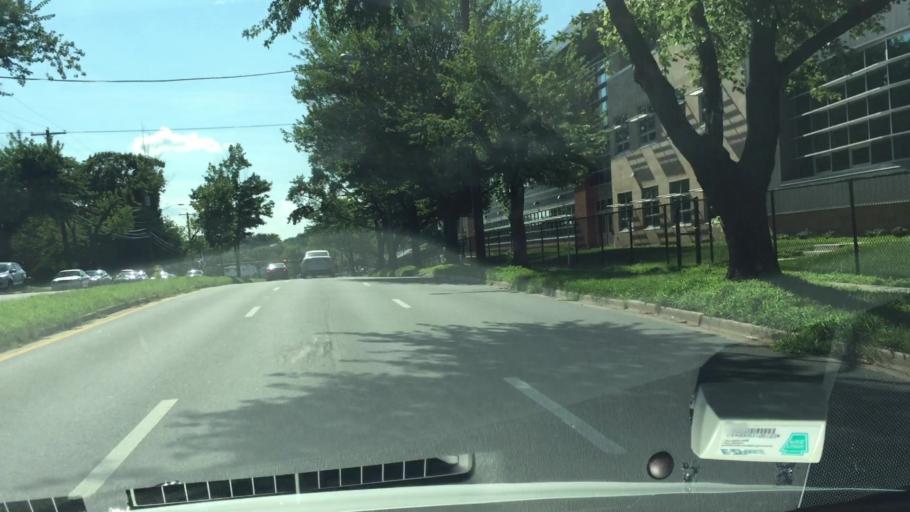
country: US
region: Maryland
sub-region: Montgomery County
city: Glenmont
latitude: 39.0592
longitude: -77.0668
